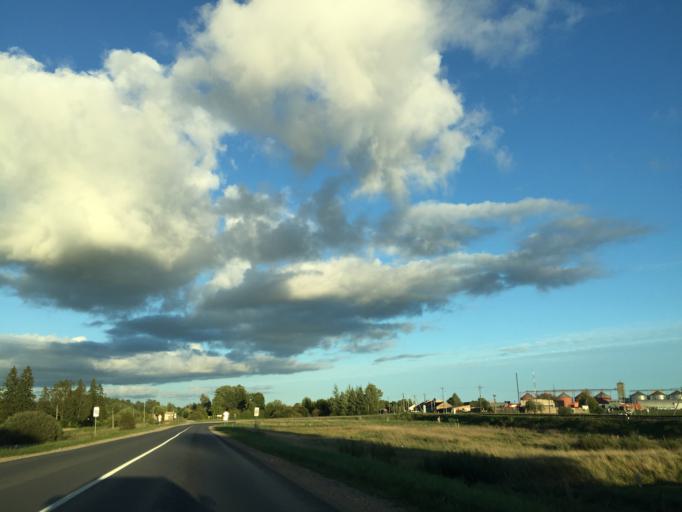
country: LV
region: Saldus Rajons
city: Saldus
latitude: 56.6891
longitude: 22.4555
